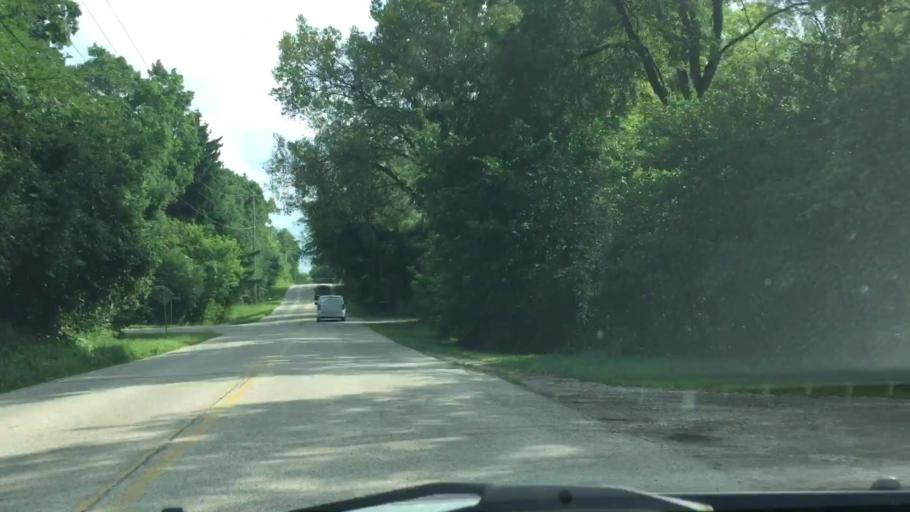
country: US
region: Wisconsin
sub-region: Waukesha County
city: Wales
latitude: 43.0461
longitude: -88.3496
